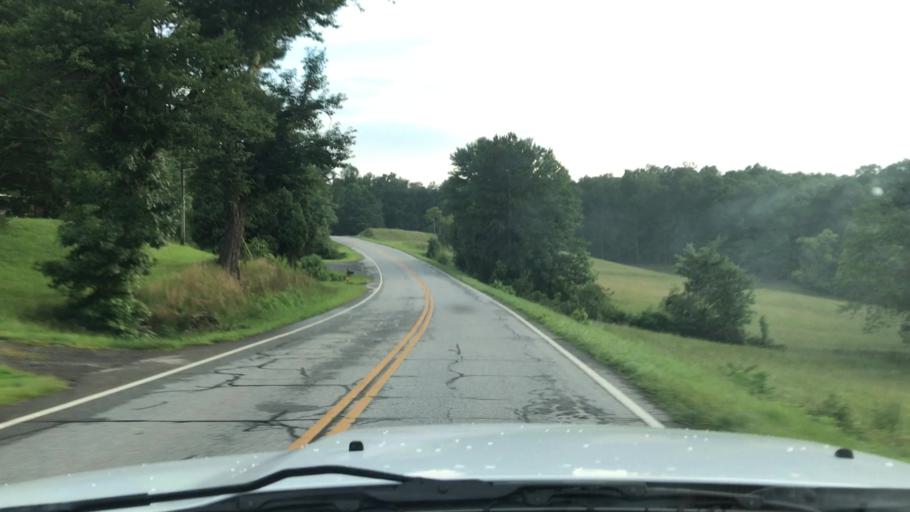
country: US
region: Georgia
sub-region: Fannin County
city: Blue Ridge
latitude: 34.9506
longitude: -84.2358
